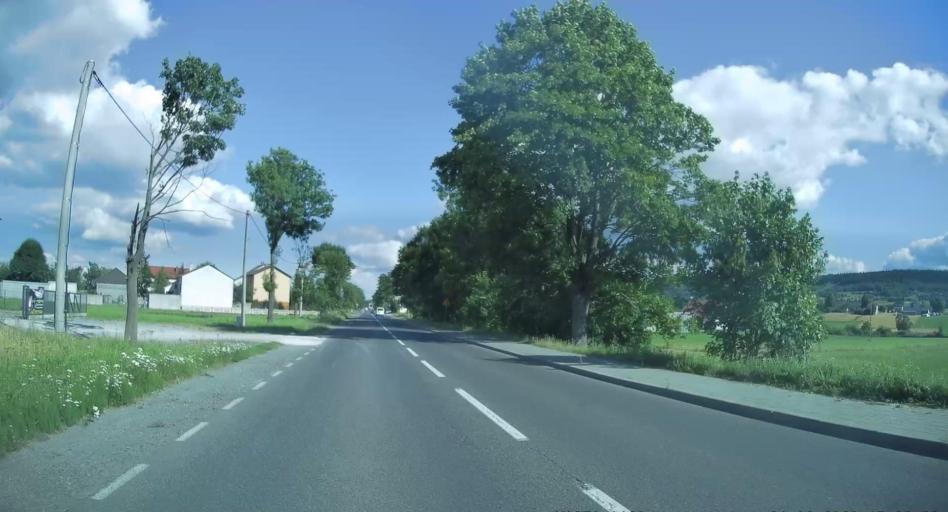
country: PL
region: Swietokrzyskie
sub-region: Powiat kielecki
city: Bodzentyn
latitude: 50.9484
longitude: 20.9324
